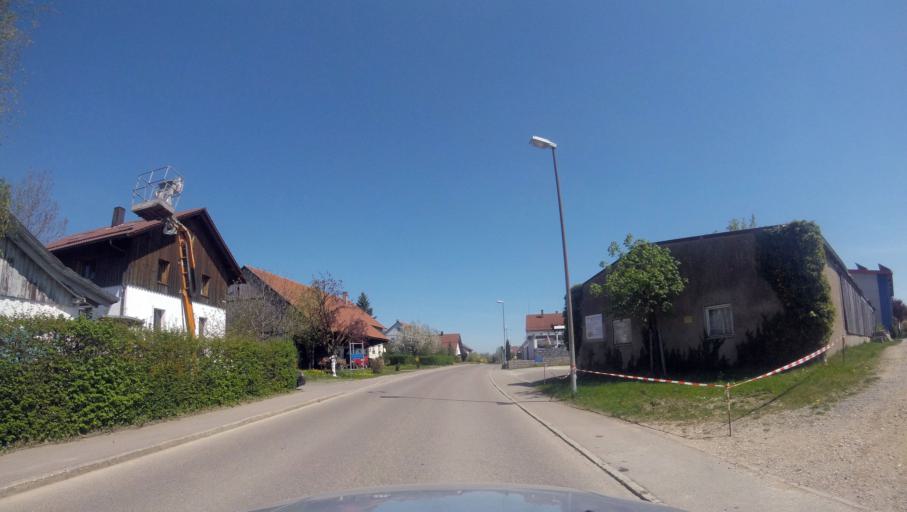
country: DE
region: Baden-Wuerttemberg
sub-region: Regierungsbezirk Stuttgart
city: Durlangen
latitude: 48.8551
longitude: 9.7906
